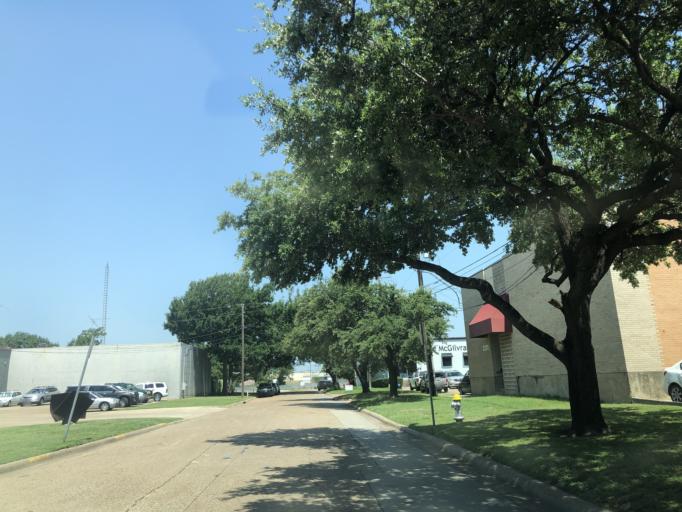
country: US
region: Texas
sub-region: Dallas County
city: Dallas
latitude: 32.8012
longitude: -96.8351
